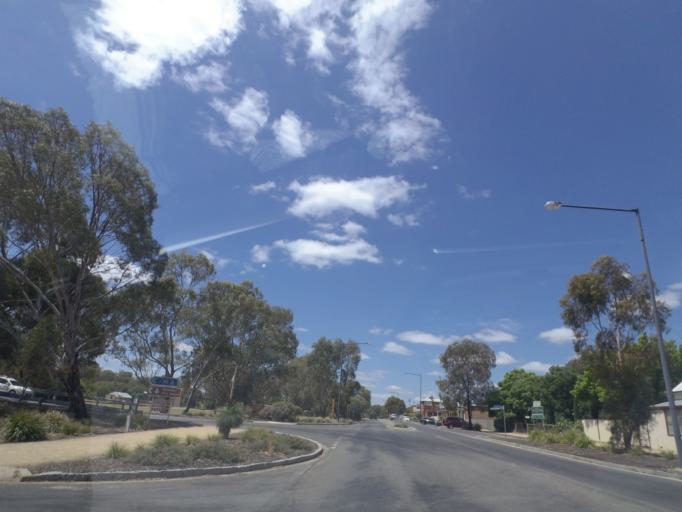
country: AU
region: Victoria
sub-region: Wangaratta
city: Wangaratta
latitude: -36.4639
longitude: 146.2226
